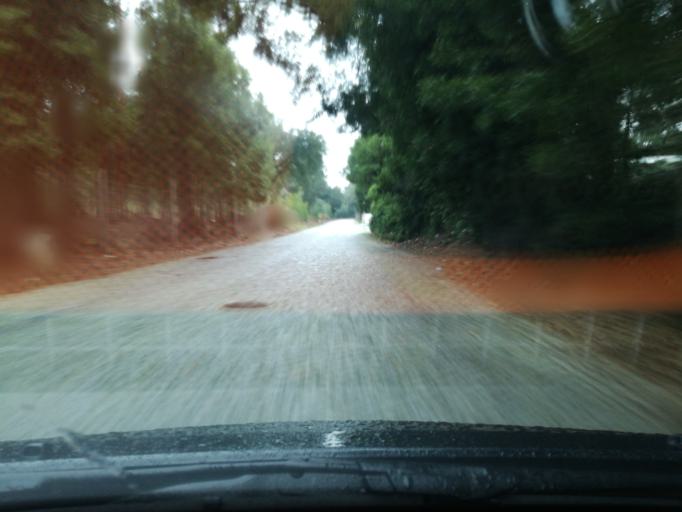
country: PT
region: Porto
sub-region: Maia
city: Gemunde
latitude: 41.2546
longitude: -8.6558
